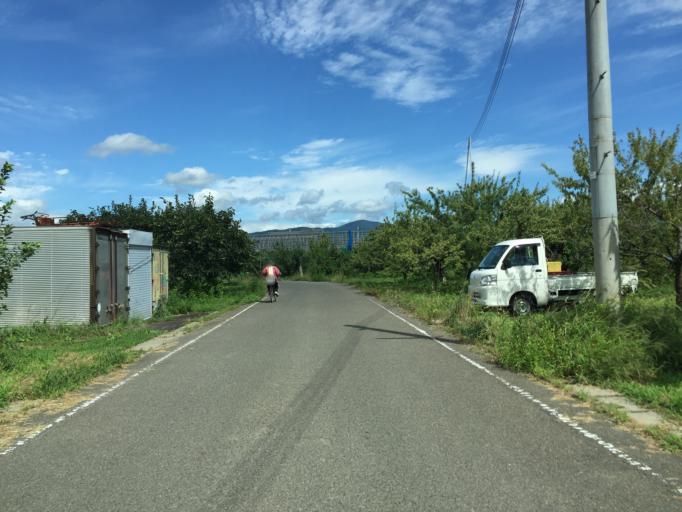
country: JP
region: Fukushima
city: Fukushima-shi
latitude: 37.7984
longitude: 140.4949
